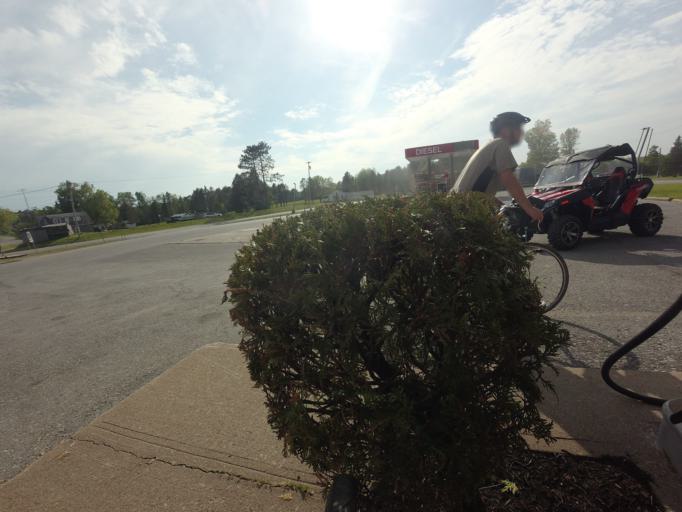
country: US
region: New York
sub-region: St. Lawrence County
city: Gouverneur
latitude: 44.1640
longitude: -75.3121
